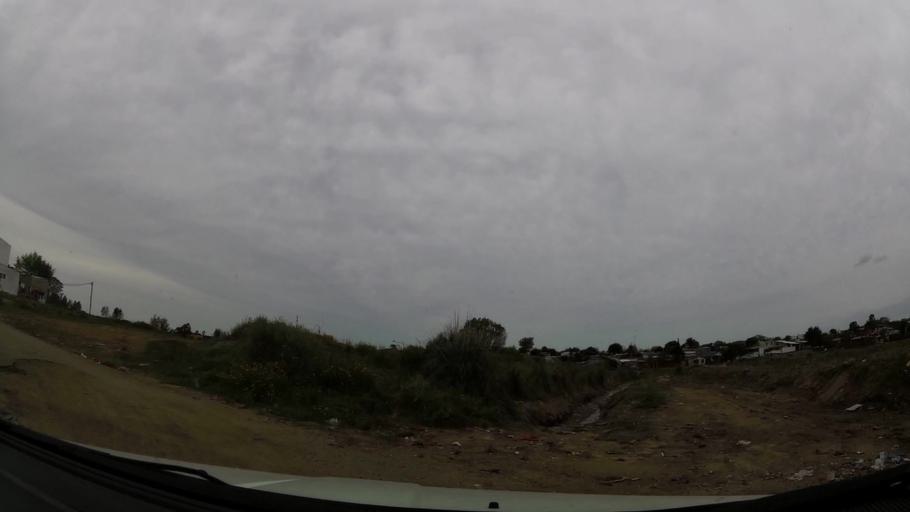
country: UY
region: Maldonado
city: Maldonado
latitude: -34.8793
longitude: -54.9776
